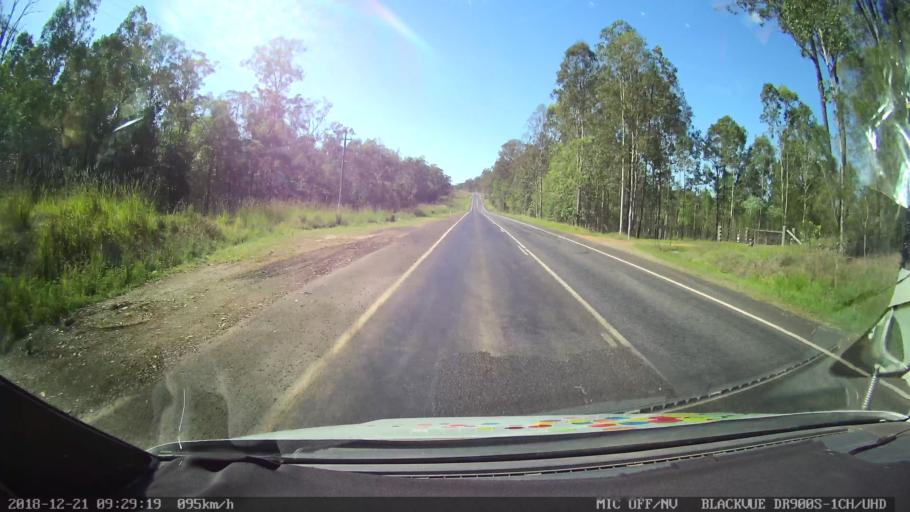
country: AU
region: New South Wales
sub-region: Clarence Valley
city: Maclean
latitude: -29.4300
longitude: 152.9891
